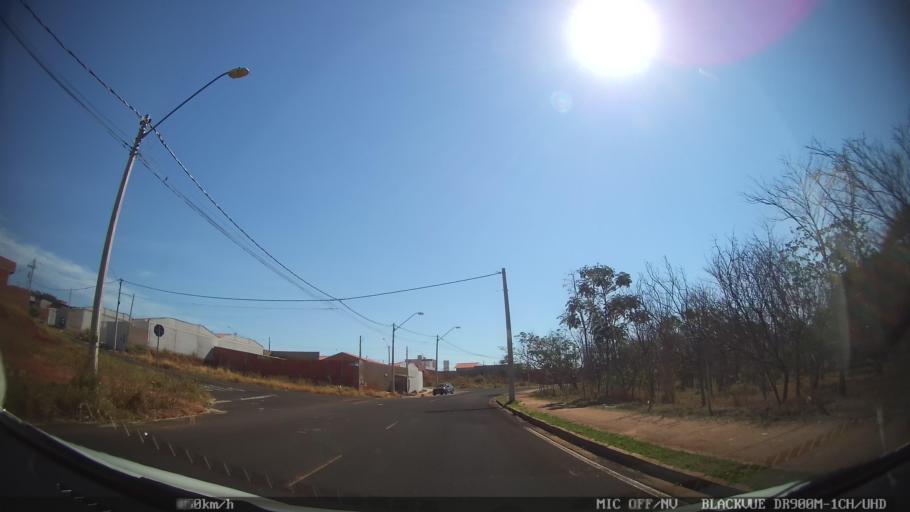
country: BR
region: Sao Paulo
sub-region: Sao Jose Do Rio Preto
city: Sao Jose do Rio Preto
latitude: -20.7530
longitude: -49.4229
